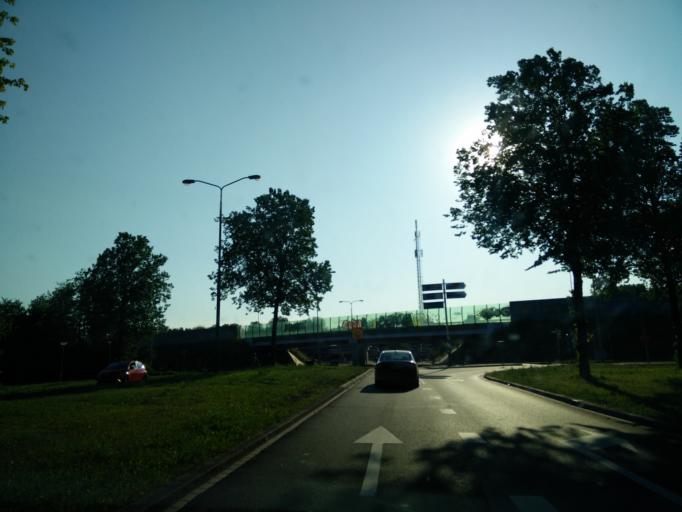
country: NL
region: South Holland
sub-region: Gemeente Dordrecht
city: Dordrecht
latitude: 51.7841
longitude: 4.6691
